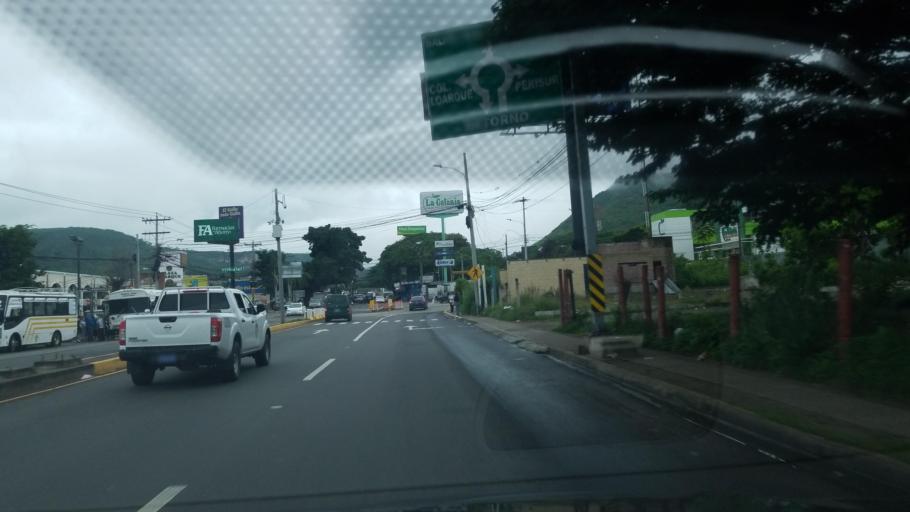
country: HN
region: Francisco Morazan
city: Yaguacire
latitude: 14.0464
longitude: -87.2122
